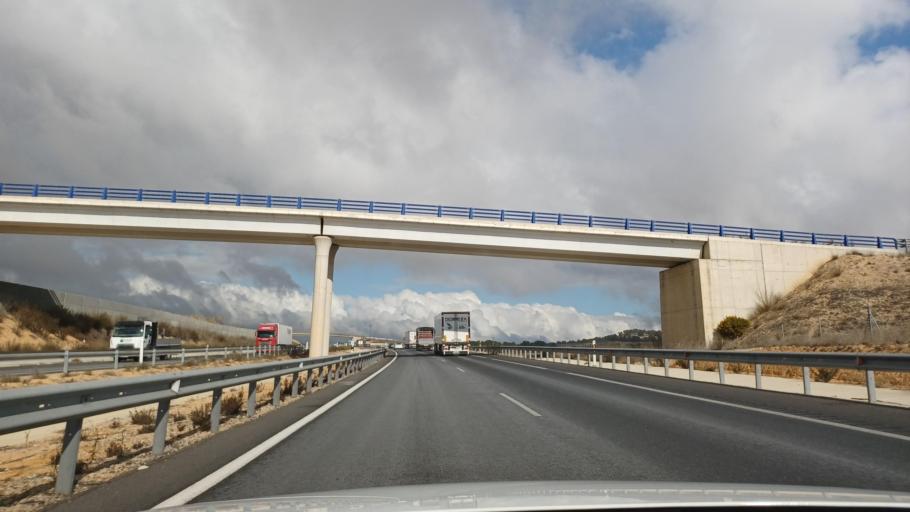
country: ES
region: Valencia
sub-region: Provincia de Valencia
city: La Font de la Figuera
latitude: 38.7621
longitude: -0.8955
